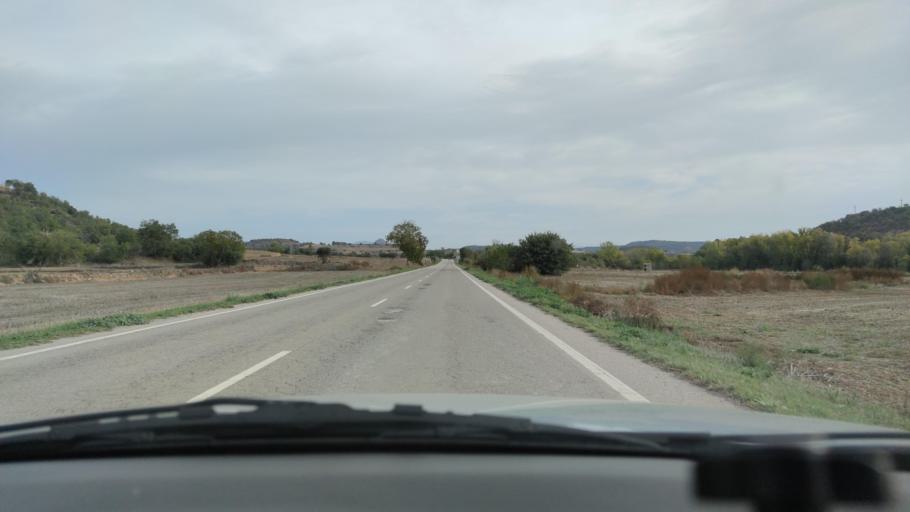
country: ES
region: Catalonia
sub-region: Provincia de Lleida
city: Artesa de Segre
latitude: 41.9138
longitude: 1.0697
